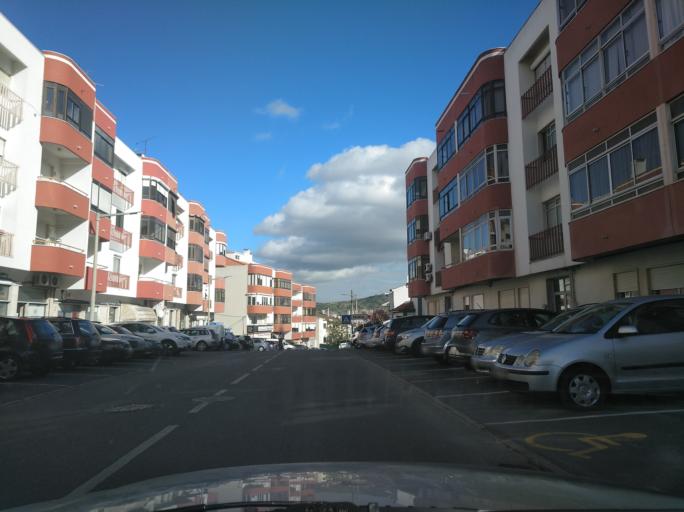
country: PT
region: Lisbon
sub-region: Loures
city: Loures
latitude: 38.8246
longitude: -9.1656
